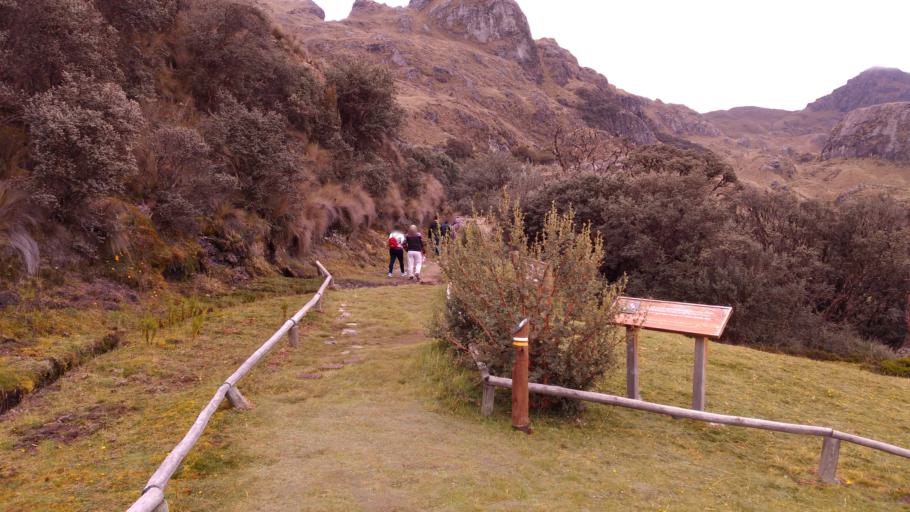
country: EC
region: Azuay
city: Cuenca
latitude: -2.7830
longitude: -79.2232
